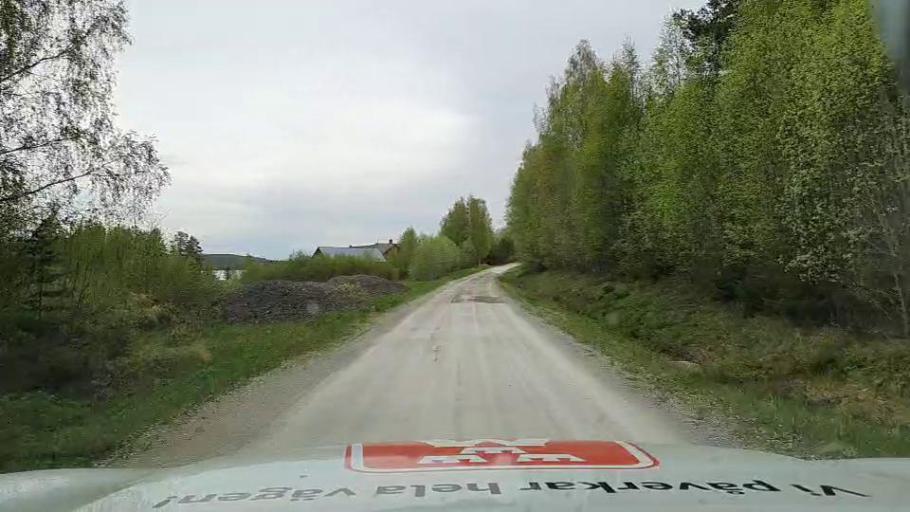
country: SE
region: Jaemtland
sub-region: Bergs Kommun
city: Hoverberg
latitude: 62.6836
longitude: 14.7744
